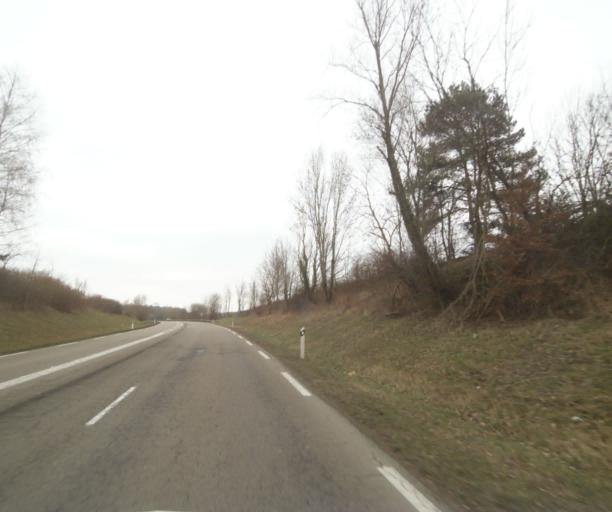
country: FR
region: Champagne-Ardenne
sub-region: Departement de la Haute-Marne
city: Bienville
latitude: 48.5835
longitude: 5.0282
